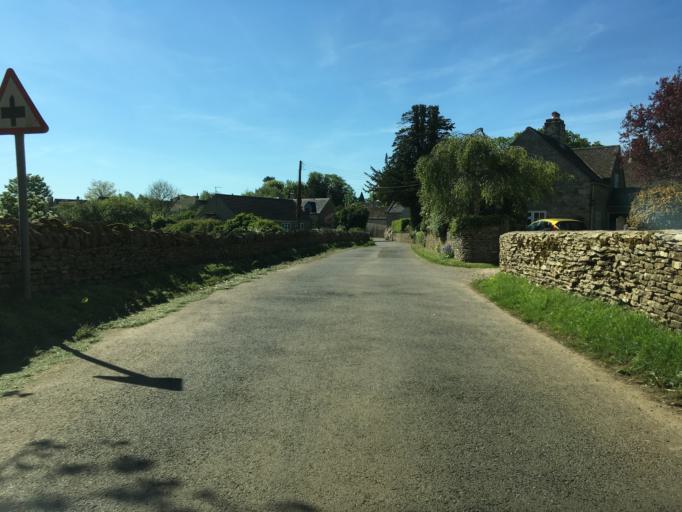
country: GB
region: England
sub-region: Wiltshire
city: Luckington
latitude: 51.6205
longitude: -2.2569
